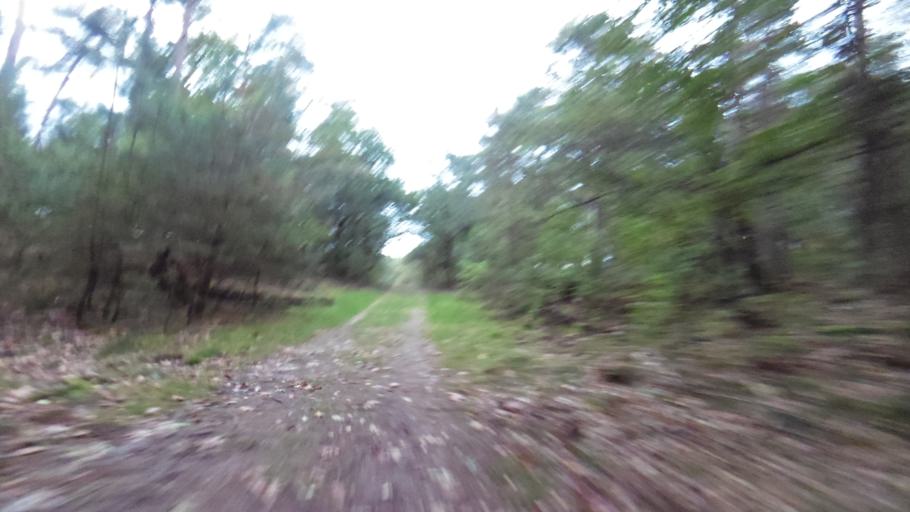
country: NL
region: Gelderland
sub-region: Gemeente Apeldoorn
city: Uddel
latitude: 52.1944
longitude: 5.7848
